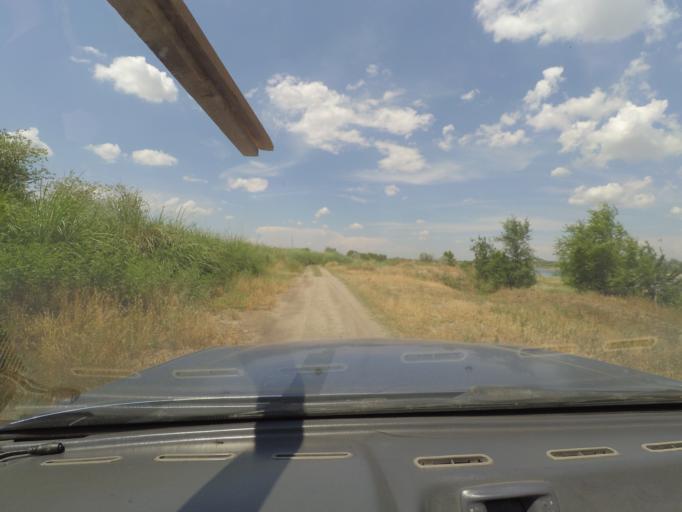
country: TJ
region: Viloyati Sughd
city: Buston
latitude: 40.5369
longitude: 69.0786
